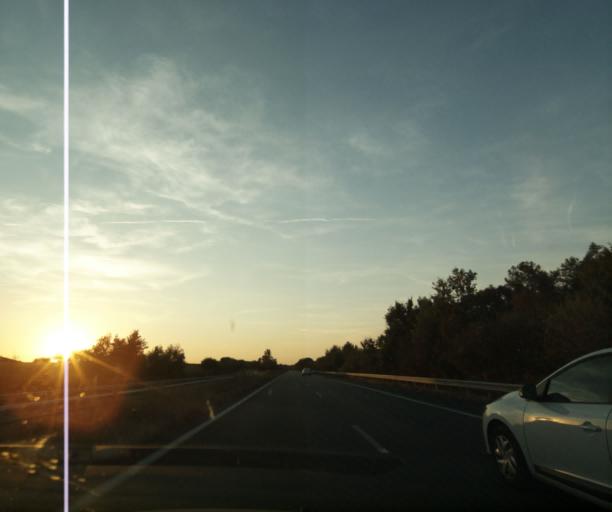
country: FR
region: Aquitaine
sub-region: Departement du Lot-et-Garonne
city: Fourques-sur-Garonne
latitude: 44.4465
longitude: 0.1017
